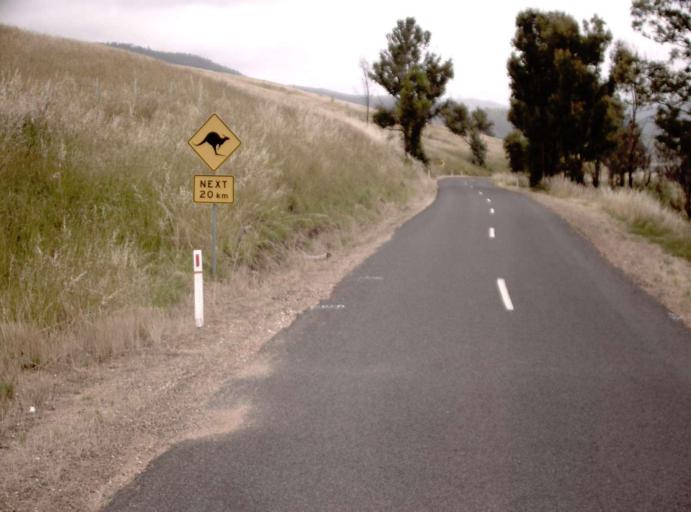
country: AU
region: Victoria
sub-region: Wellington
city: Heyfield
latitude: -37.8241
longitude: 146.6756
